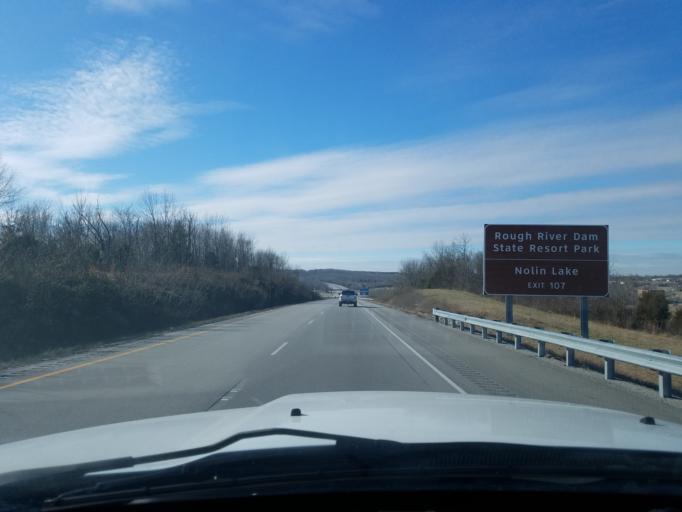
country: US
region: Kentucky
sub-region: Grayson County
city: Leitchfield
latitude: 37.4676
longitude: -86.2794
